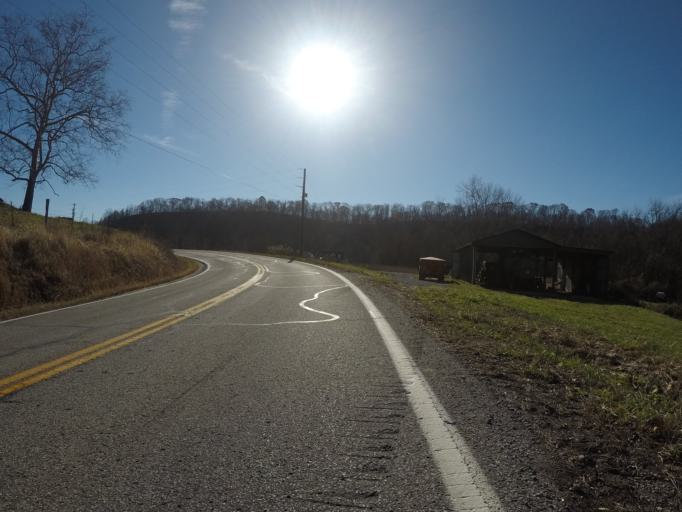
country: US
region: West Virginia
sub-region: Cabell County
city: Huntington
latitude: 38.4686
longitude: -82.4460
